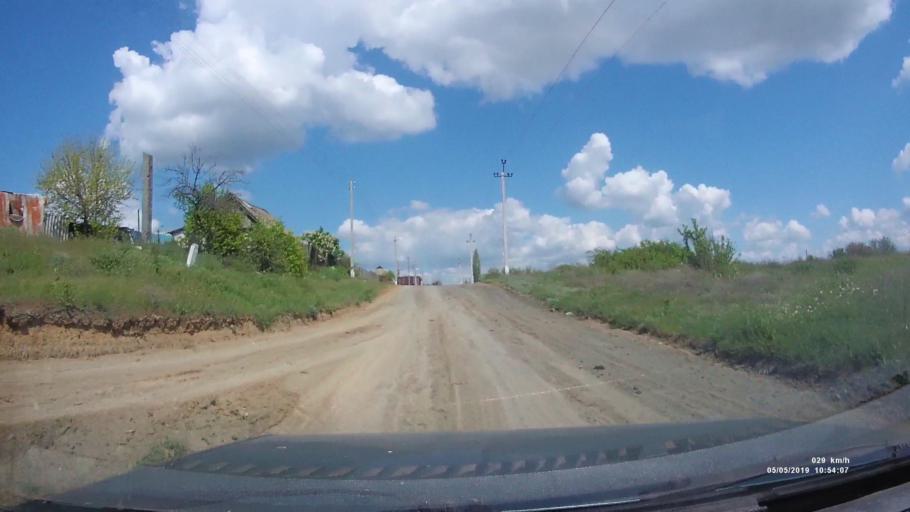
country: RU
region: Rostov
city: Ust'-Donetskiy
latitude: 47.6567
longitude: 40.8235
